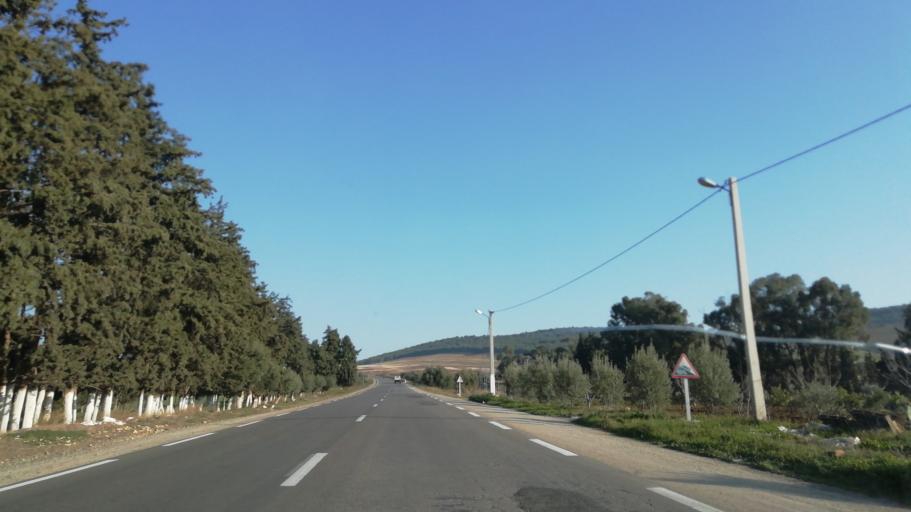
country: DZ
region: Ain Temouchent
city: Hammam Bou Hadjar
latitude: 35.1677
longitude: -0.8964
